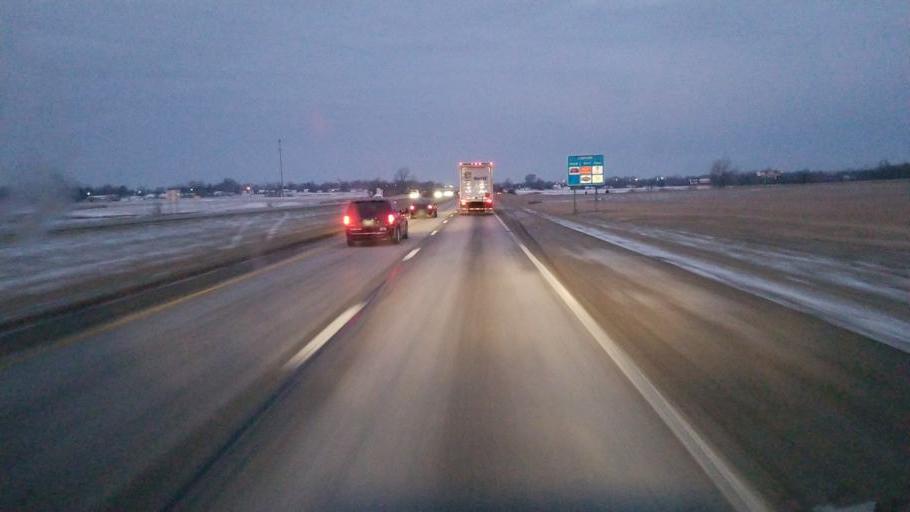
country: US
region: Ohio
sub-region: Preble County
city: New Paris
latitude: 39.8288
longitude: -84.7818
